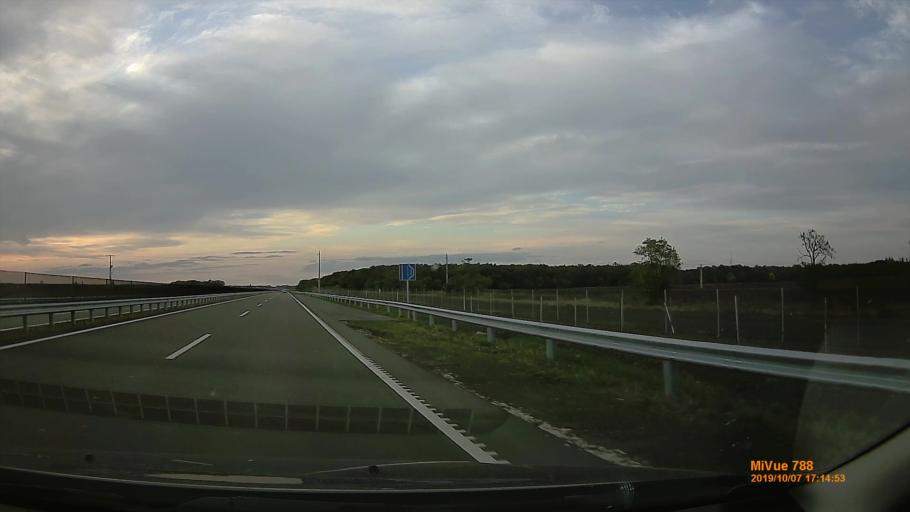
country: HU
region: Jasz-Nagykun-Szolnok
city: Kunszentmarton
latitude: 46.8390
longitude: 20.3404
